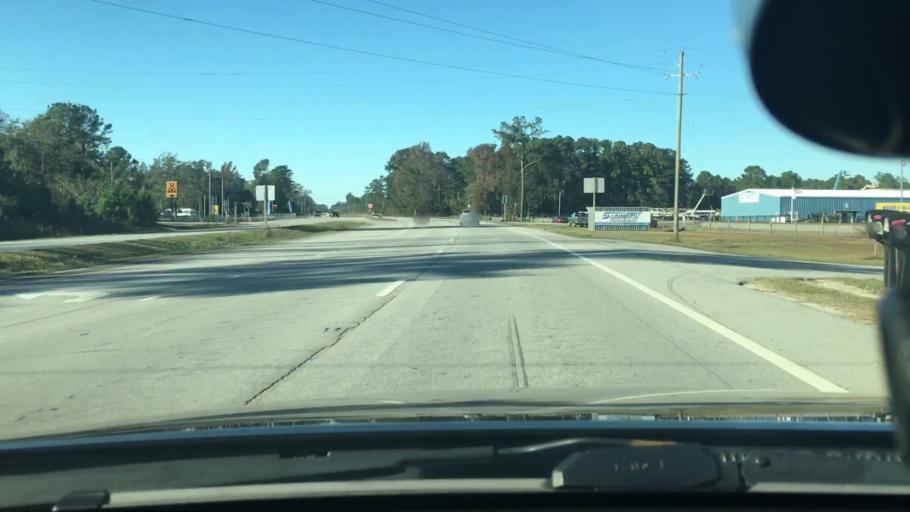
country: US
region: North Carolina
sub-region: Craven County
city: New Bern
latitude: 35.1343
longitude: -77.0266
